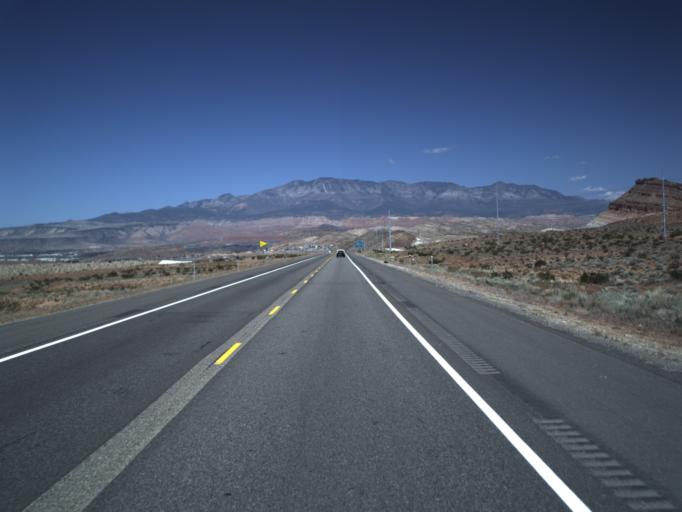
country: US
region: Utah
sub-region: Washington County
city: Washington
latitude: 37.0462
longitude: -113.4857
